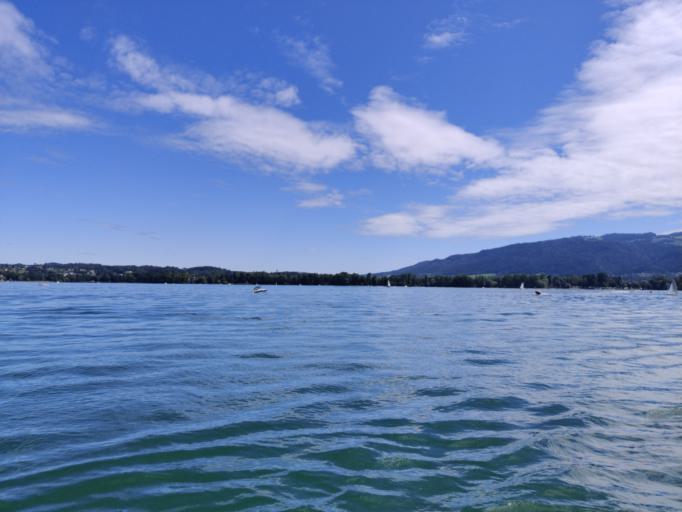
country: DE
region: Bavaria
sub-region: Swabia
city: Lindau
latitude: 47.5321
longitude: 9.7138
